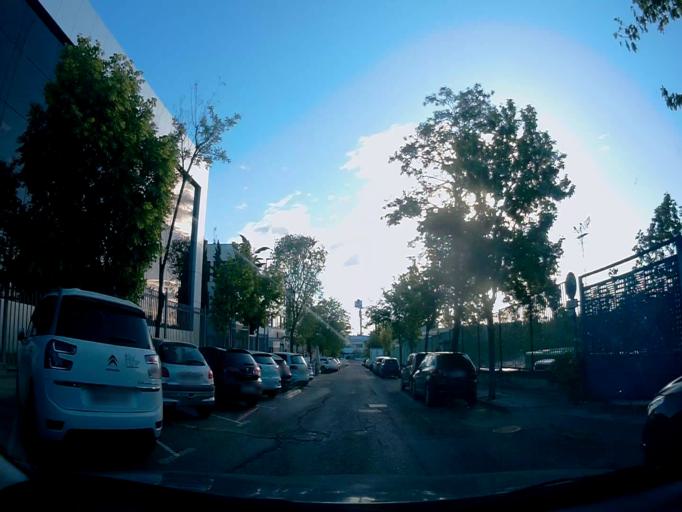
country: ES
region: Madrid
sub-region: Provincia de Madrid
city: San Sebastian de los Reyes
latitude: 40.5587
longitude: -3.6228
